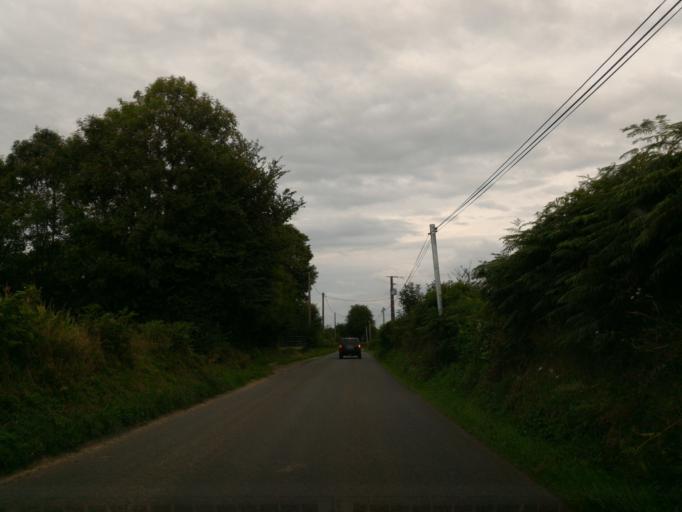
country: FR
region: Lower Normandy
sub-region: Departement de la Manche
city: Sartilly
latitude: 48.7816
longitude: -1.4687
